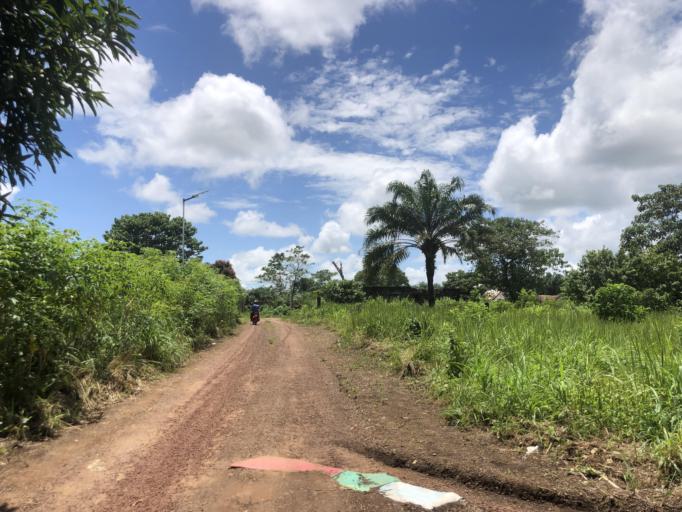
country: SL
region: Northern Province
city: Makeni
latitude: 8.8576
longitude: -12.0472
